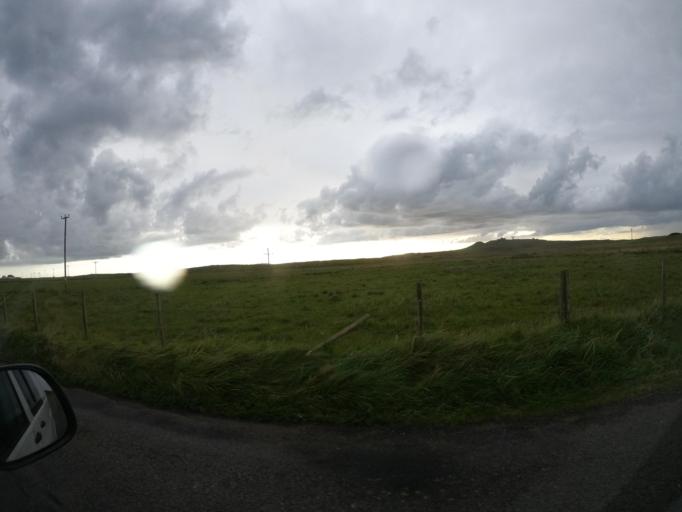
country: GB
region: Scotland
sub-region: Eilean Siar
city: Barra
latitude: 56.5071
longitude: -6.8092
